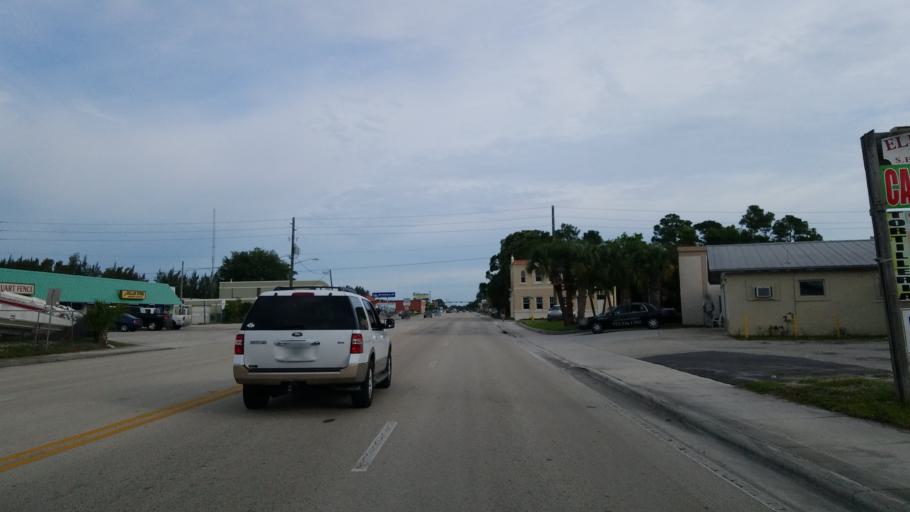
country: US
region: Florida
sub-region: Martin County
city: Port Salerno
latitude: 27.1648
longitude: -80.2186
